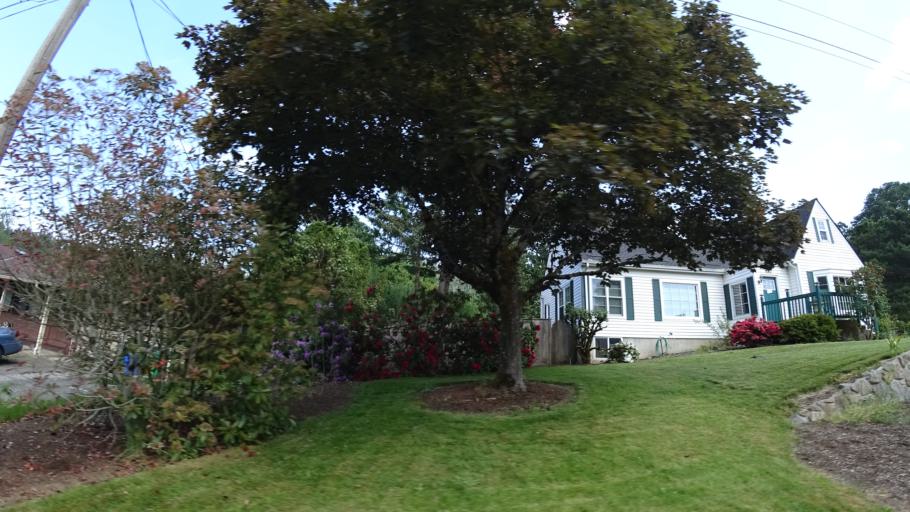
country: US
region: Oregon
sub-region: Washington County
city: Metzger
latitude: 45.4467
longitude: -122.7367
